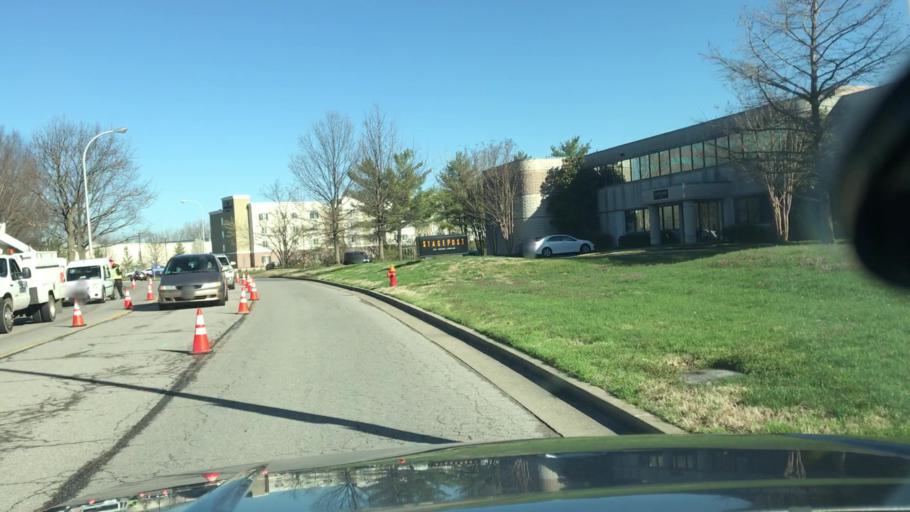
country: US
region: Tennessee
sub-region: Davidson County
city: Nashville
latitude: 36.1945
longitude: -86.7966
